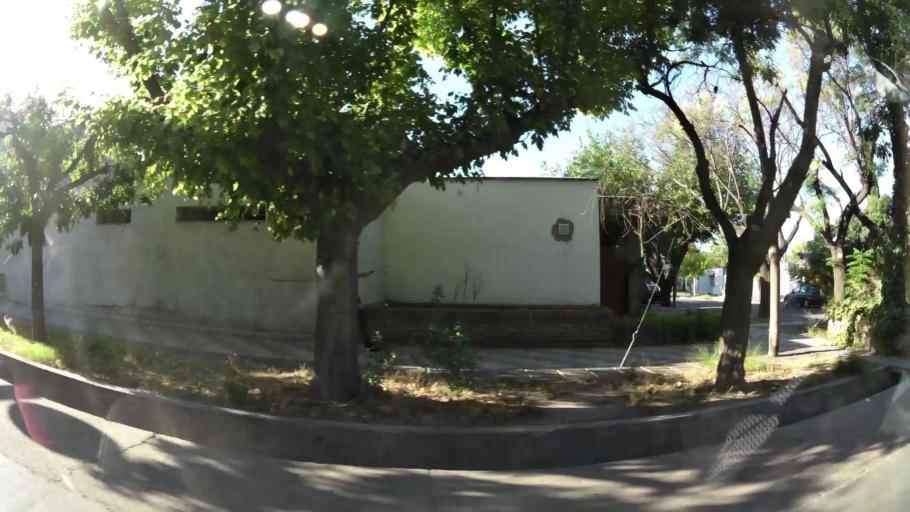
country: AR
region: Mendoza
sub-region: Departamento de Godoy Cruz
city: Godoy Cruz
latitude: -32.9126
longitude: -68.8359
